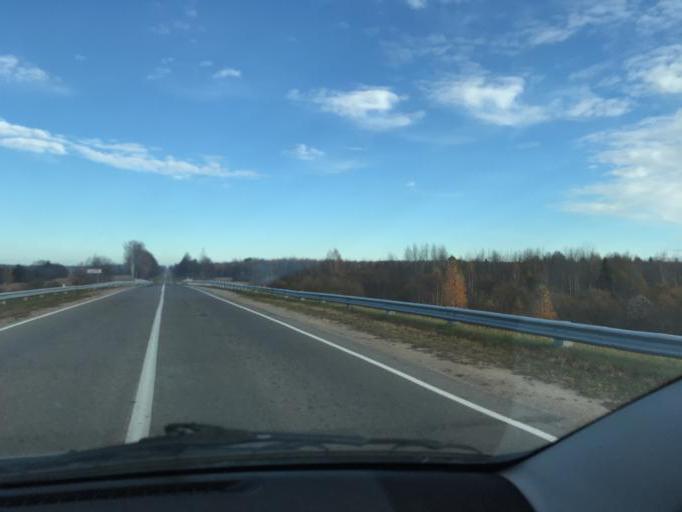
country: BY
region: Vitebsk
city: Haradok
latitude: 55.5013
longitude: 29.9679
